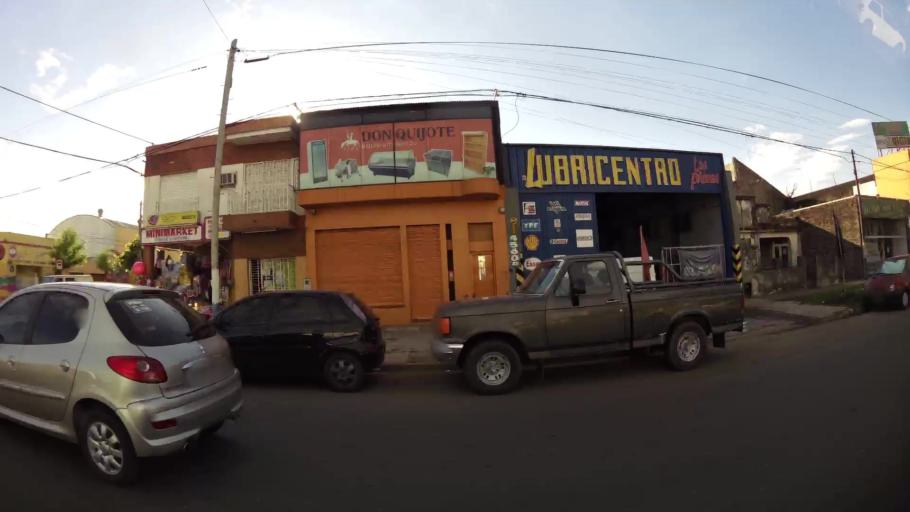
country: AR
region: Santa Fe
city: Gobernador Galvez
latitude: -32.9897
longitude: -60.6729
